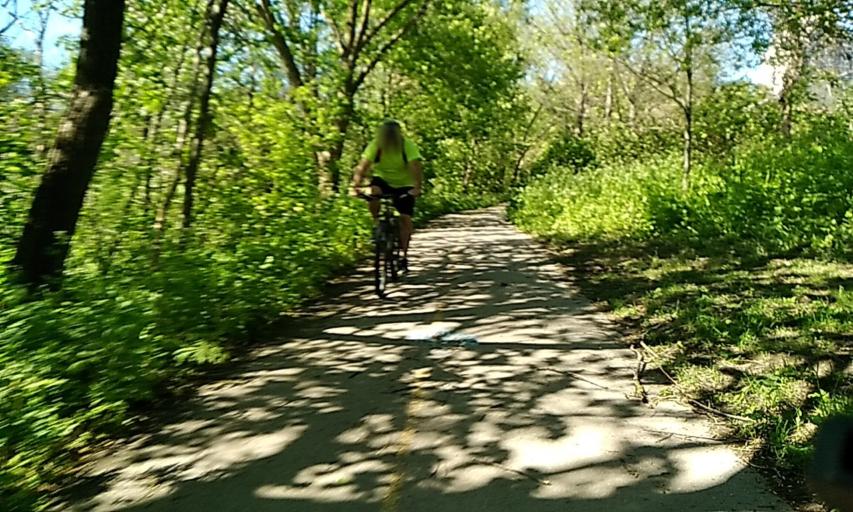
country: CA
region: Ontario
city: London
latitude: 42.9776
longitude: -81.2555
